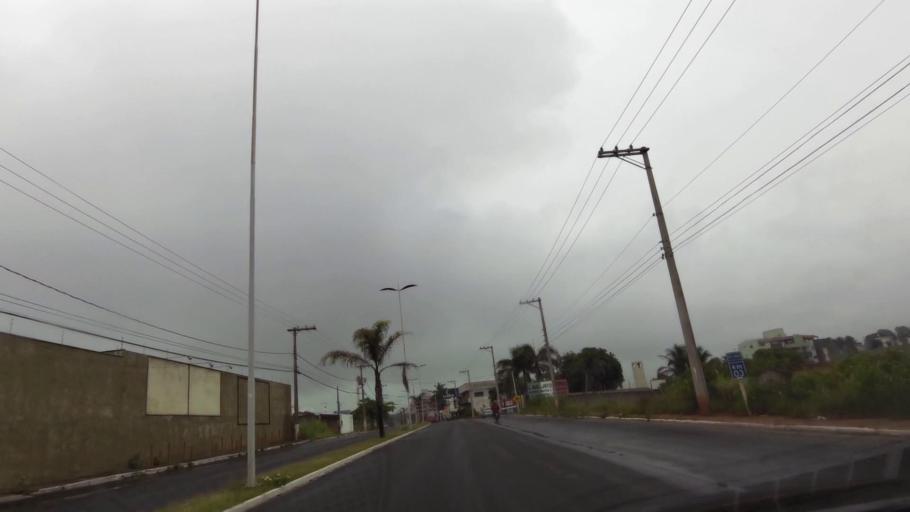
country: BR
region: Espirito Santo
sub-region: Guarapari
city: Guarapari
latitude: -20.7270
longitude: -40.5290
